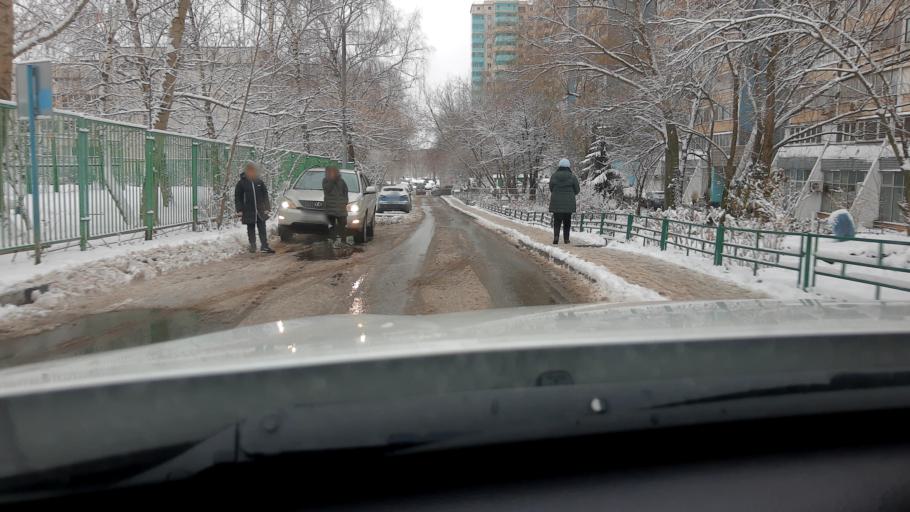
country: RU
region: Moscow
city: Yasenevo
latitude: 55.6003
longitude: 37.5326
